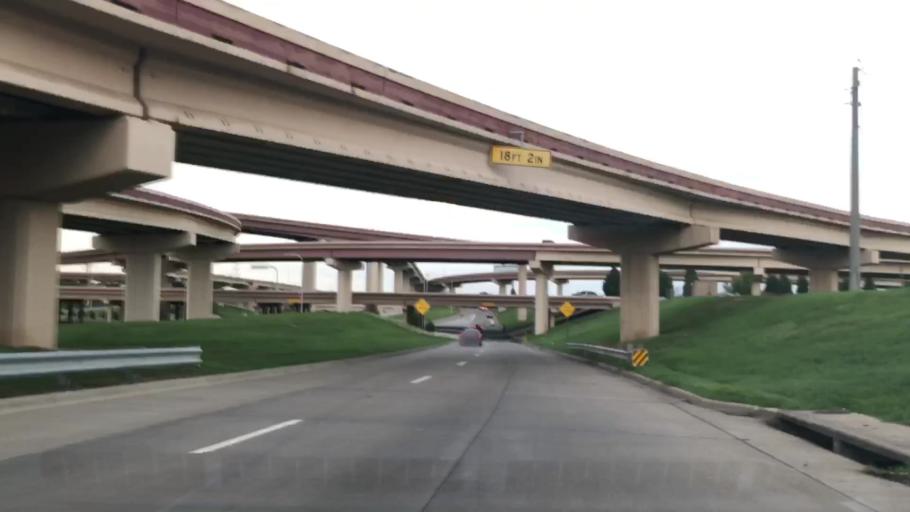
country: US
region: Texas
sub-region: Dallas County
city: Addison
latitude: 33.0111
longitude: -96.8285
